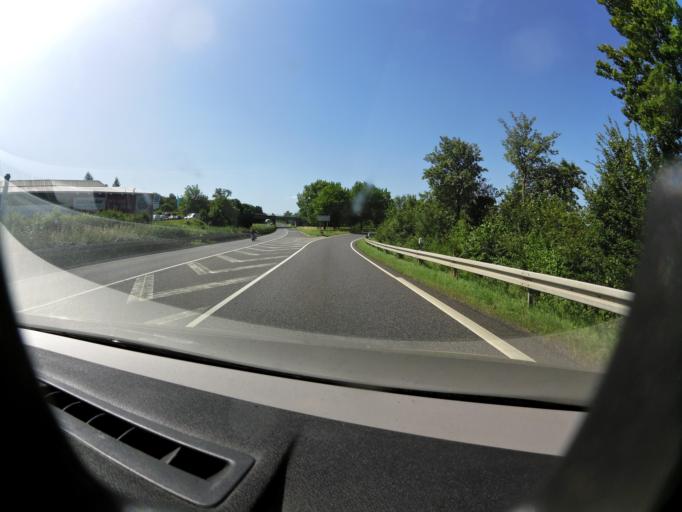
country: DE
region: Hesse
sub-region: Regierungsbezirk Kassel
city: Petersberg
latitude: 50.5712
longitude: 9.6946
